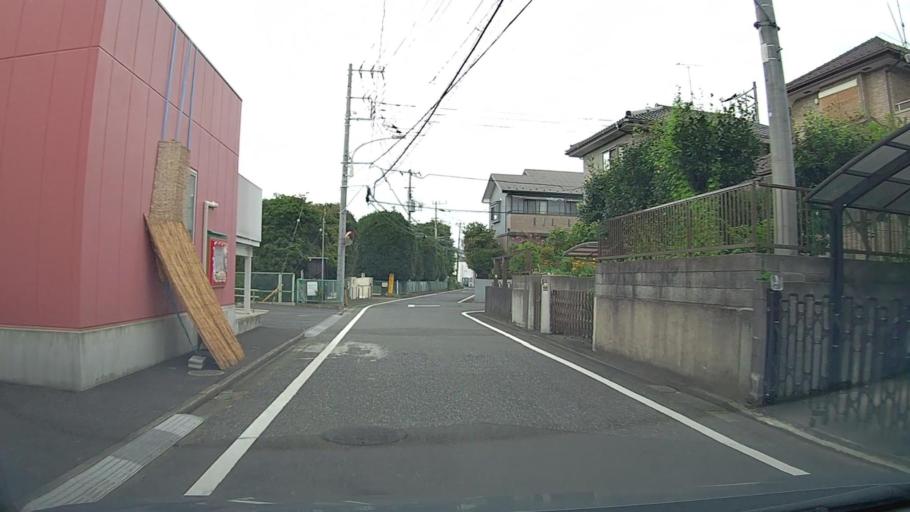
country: JP
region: Tokyo
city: Higashimurayama-shi
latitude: 35.7518
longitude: 139.4888
